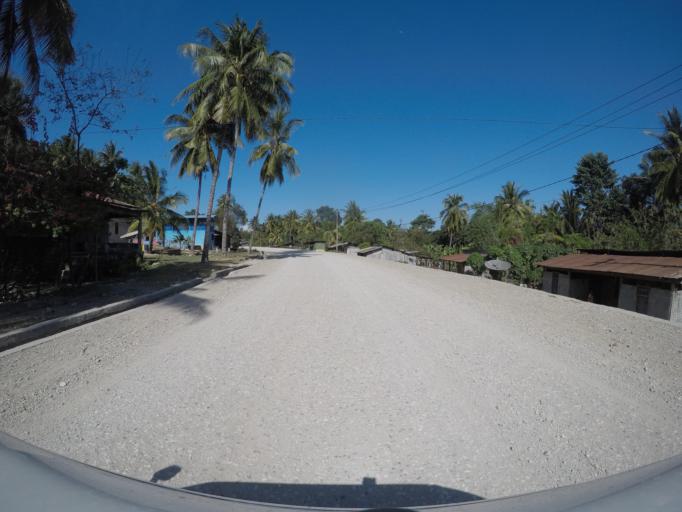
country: TL
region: Viqueque
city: Viqueque
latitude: -8.8425
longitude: 126.5149
